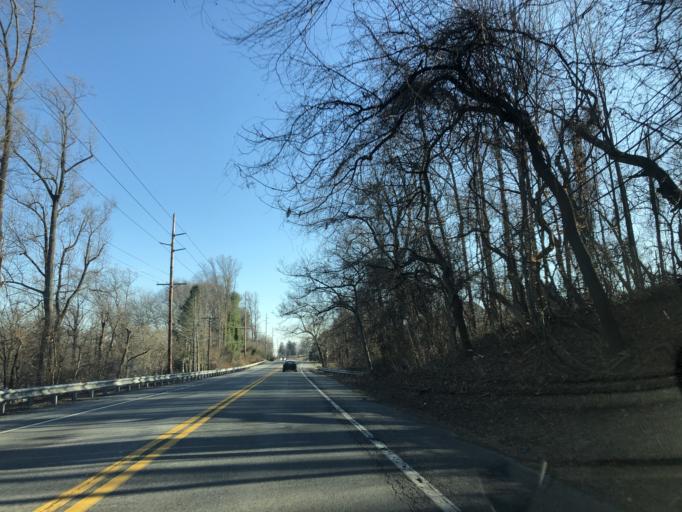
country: US
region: Delaware
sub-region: New Castle County
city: Pike Creek Valley
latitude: 39.7579
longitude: -75.6571
